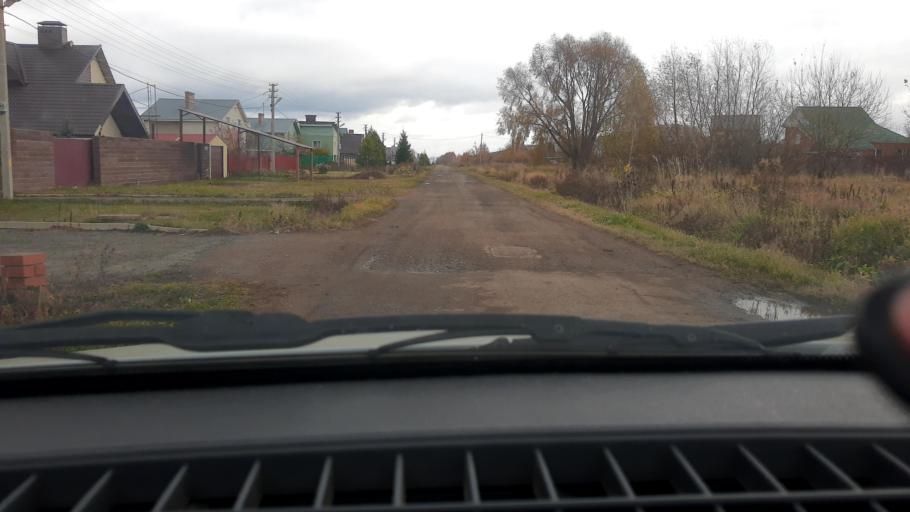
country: RU
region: Bashkortostan
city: Avdon
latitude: 54.6902
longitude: 55.7854
